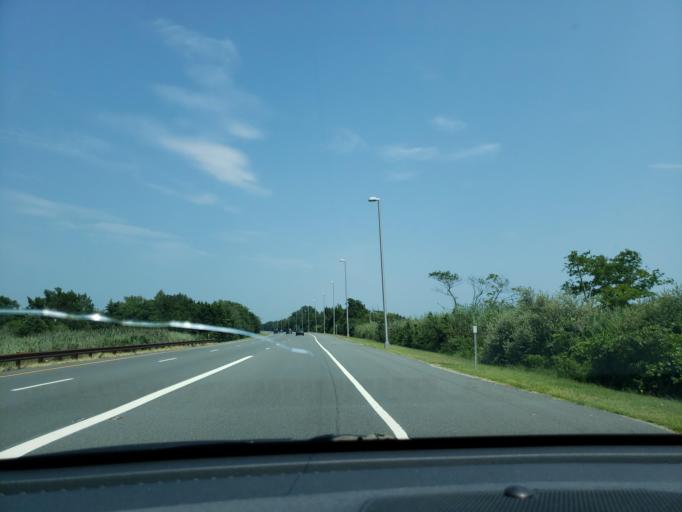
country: US
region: New Jersey
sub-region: Cape May County
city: Sea Isle City
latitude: 39.1955
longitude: -74.7075
